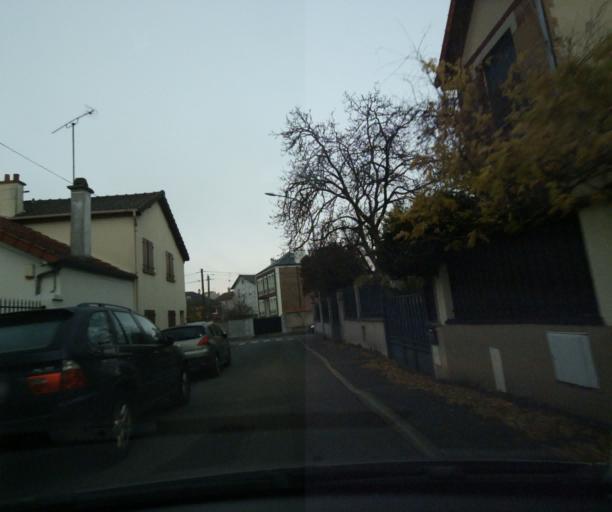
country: FR
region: Ile-de-France
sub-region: Departement du Val-de-Marne
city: Le Perreux-sur-Marne
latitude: 48.8561
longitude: 2.5018
